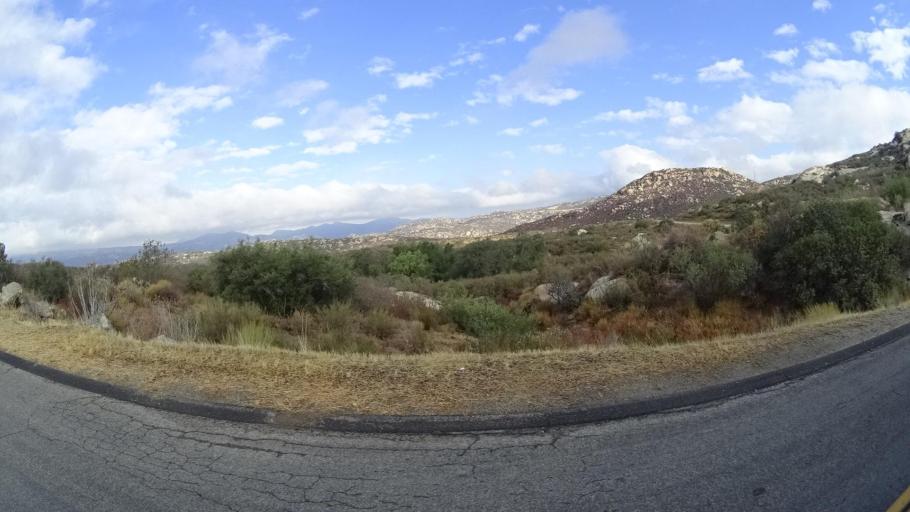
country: MX
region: Baja California
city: Tecate
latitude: 32.6416
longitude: -116.6362
